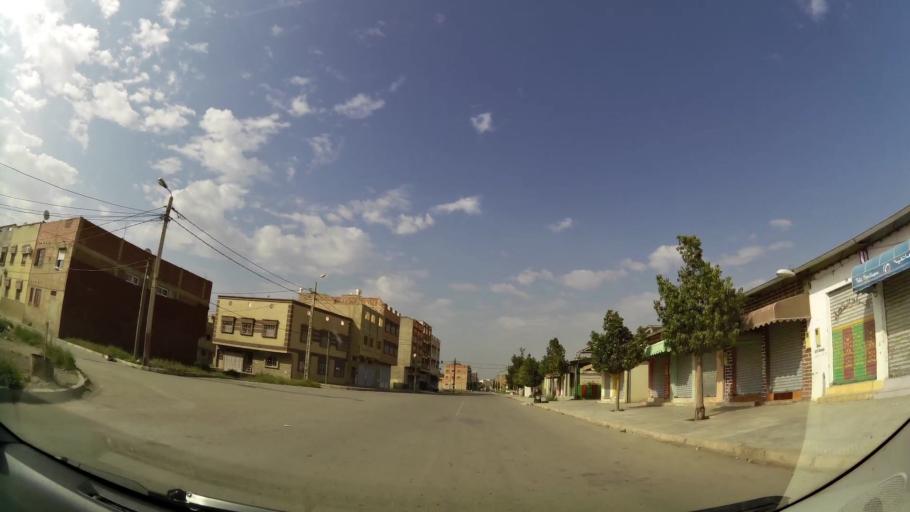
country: MA
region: Oriental
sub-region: Oujda-Angad
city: Oujda
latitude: 34.6892
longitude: -1.8995
